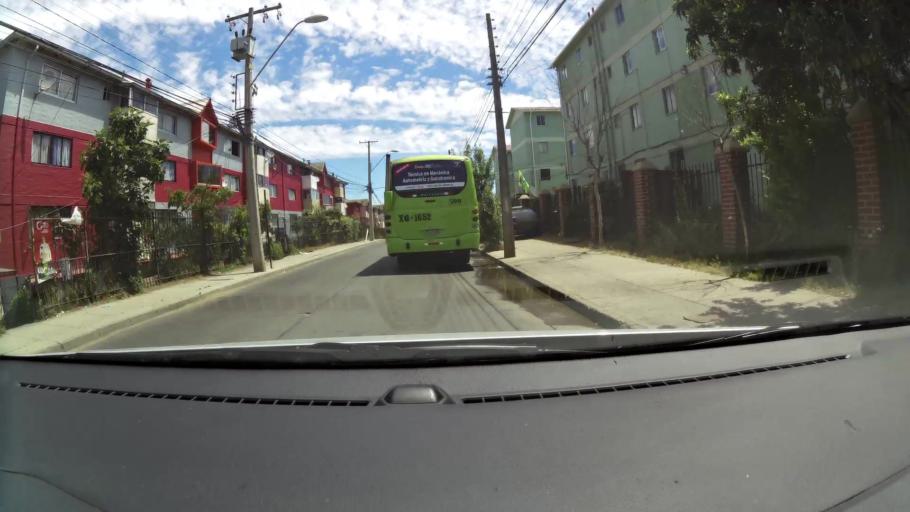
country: CL
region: Valparaiso
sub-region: Provincia de Valparaiso
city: Vina del Mar
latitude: -33.0658
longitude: -71.5666
